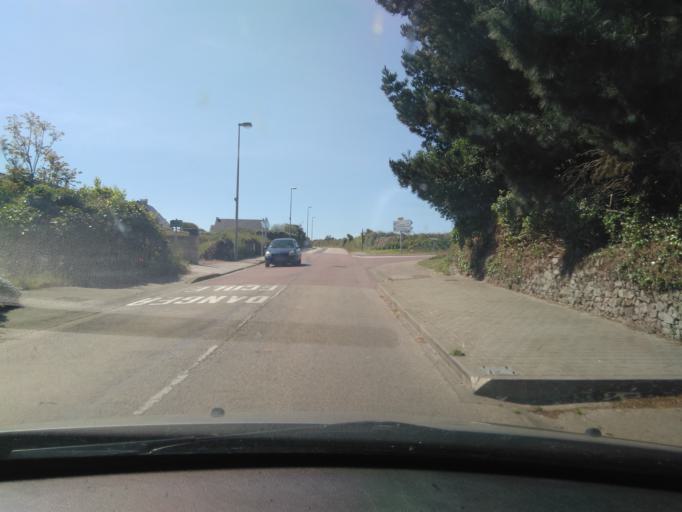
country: FR
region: Lower Normandy
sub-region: Departement de la Manche
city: Beaumont-Hague
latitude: 49.7096
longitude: -1.9321
